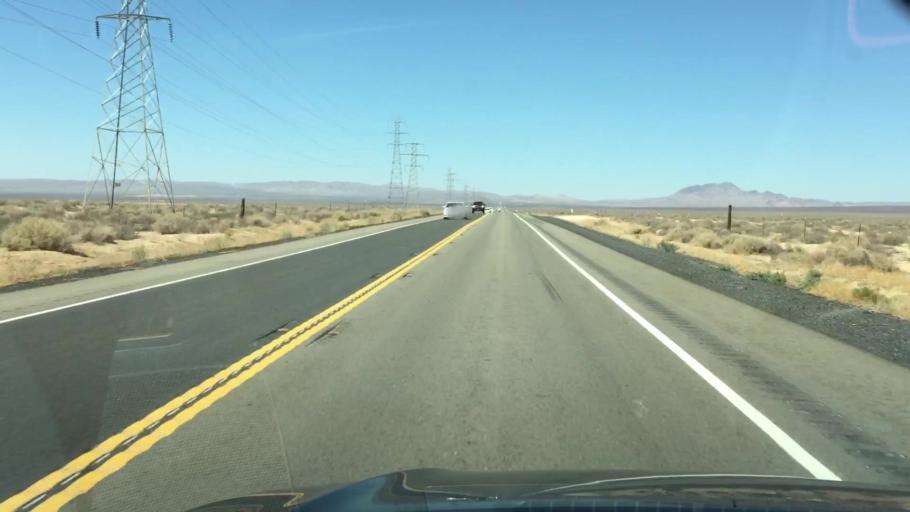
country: US
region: California
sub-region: Kern County
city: Boron
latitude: 35.1473
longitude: -117.5846
